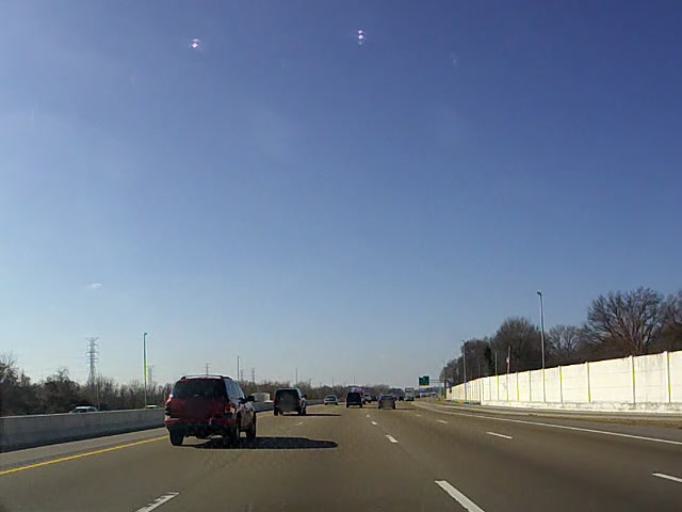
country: US
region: Tennessee
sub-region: Shelby County
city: Germantown
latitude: 35.0780
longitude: -89.9109
